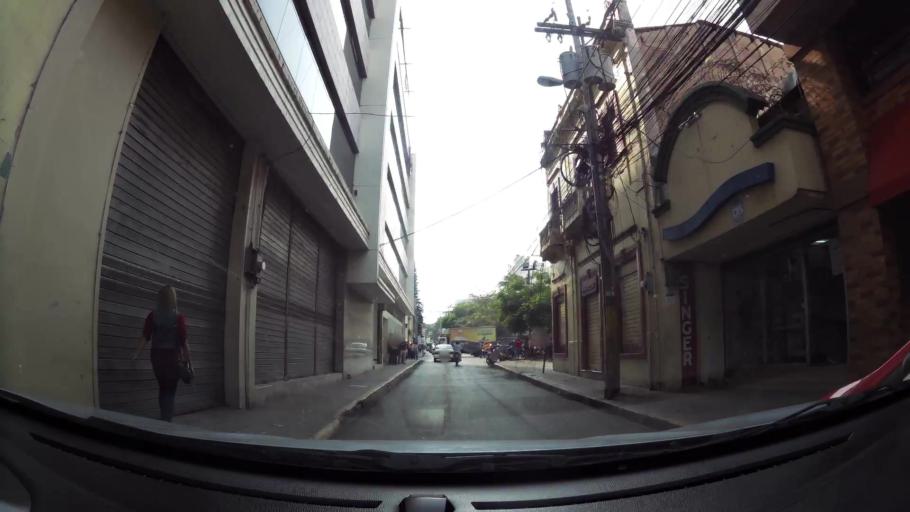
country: HN
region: Francisco Morazan
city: Tegucigalpa
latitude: 14.1064
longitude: -87.2052
